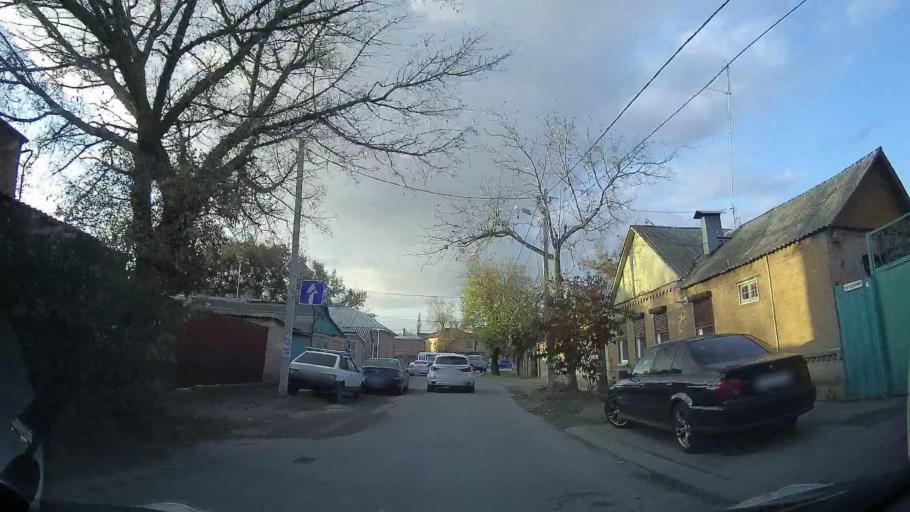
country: RU
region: Rostov
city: Imeni Chkalova
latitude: 47.2478
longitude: 39.7770
